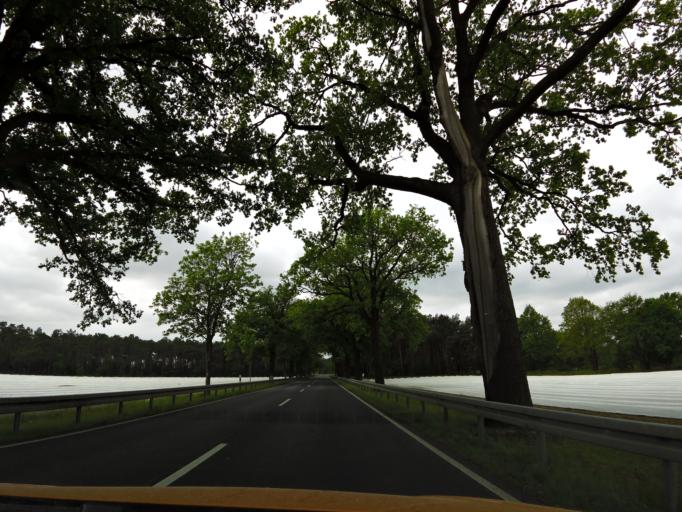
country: DE
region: Brandenburg
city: Beelitz
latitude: 52.1770
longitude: 12.9361
